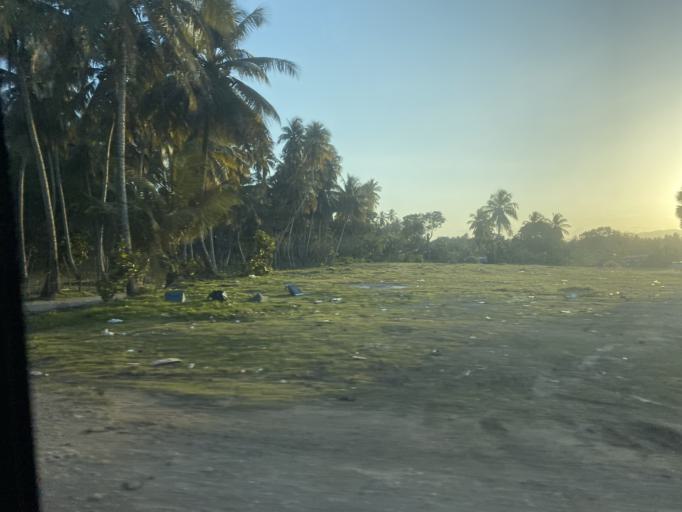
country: DO
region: Maria Trinidad Sanchez
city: Nagua
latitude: 19.3649
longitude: -69.8364
